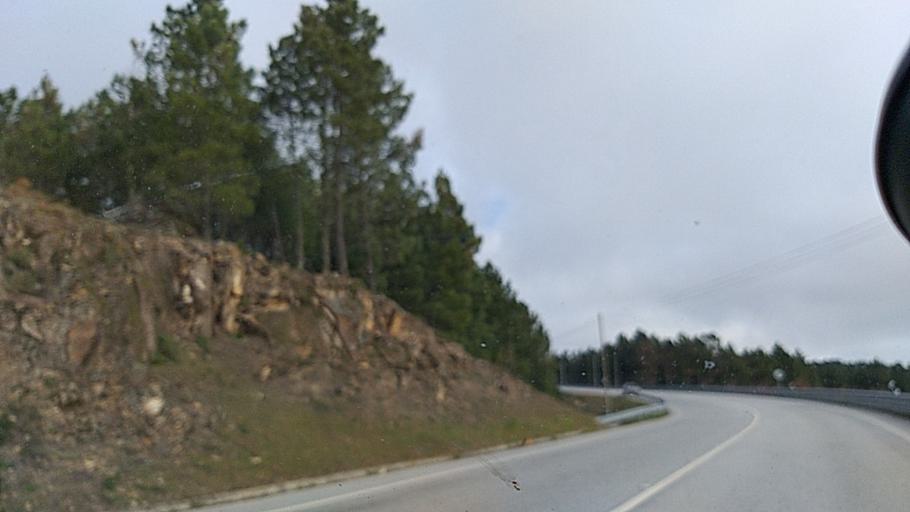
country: PT
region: Guarda
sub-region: Aguiar da Beira
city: Aguiar da Beira
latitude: 40.7844
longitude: -7.5026
